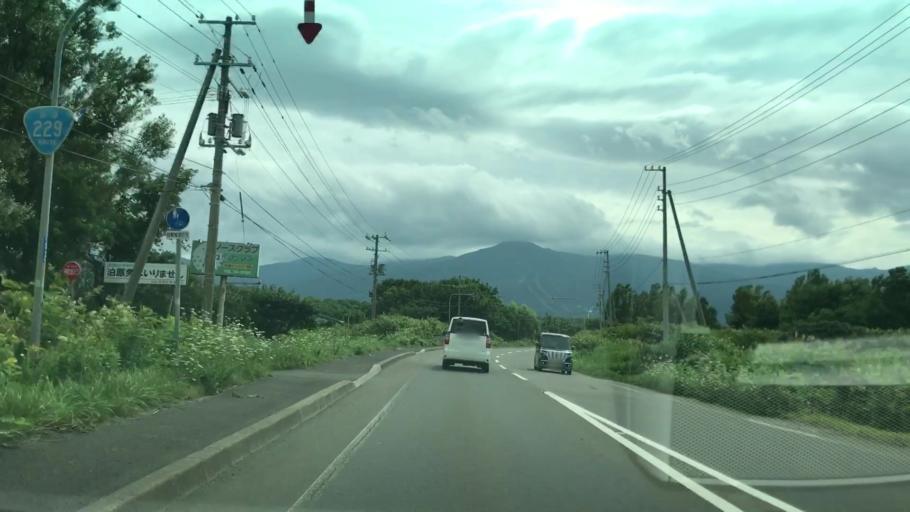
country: JP
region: Hokkaido
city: Iwanai
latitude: 43.0053
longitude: 140.5425
